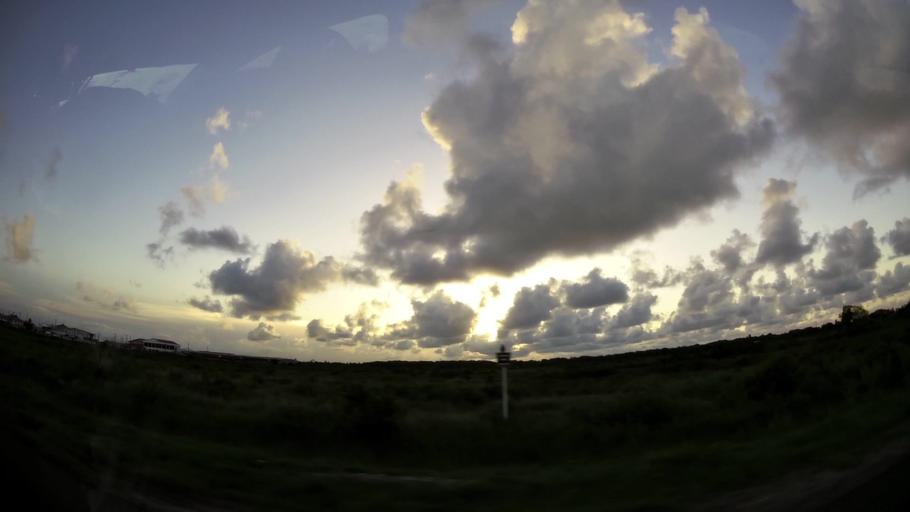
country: GY
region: Demerara-Mahaica
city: Georgetown
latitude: 6.8088
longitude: -58.1005
